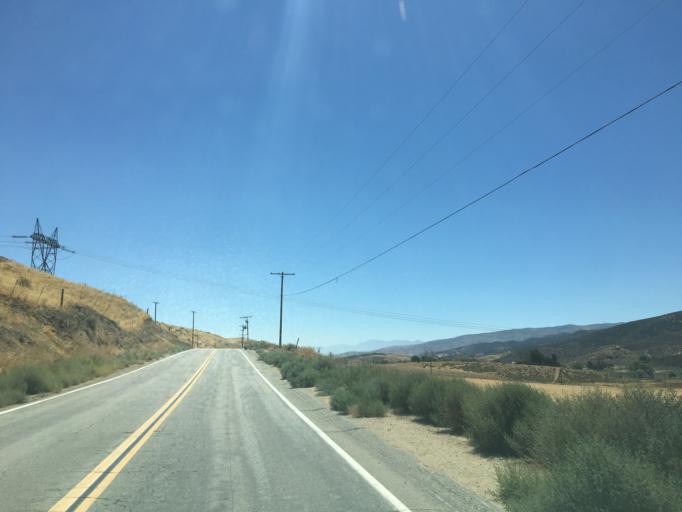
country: US
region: California
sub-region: Los Angeles County
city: Leona Valley
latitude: 34.6377
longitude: -118.3450
